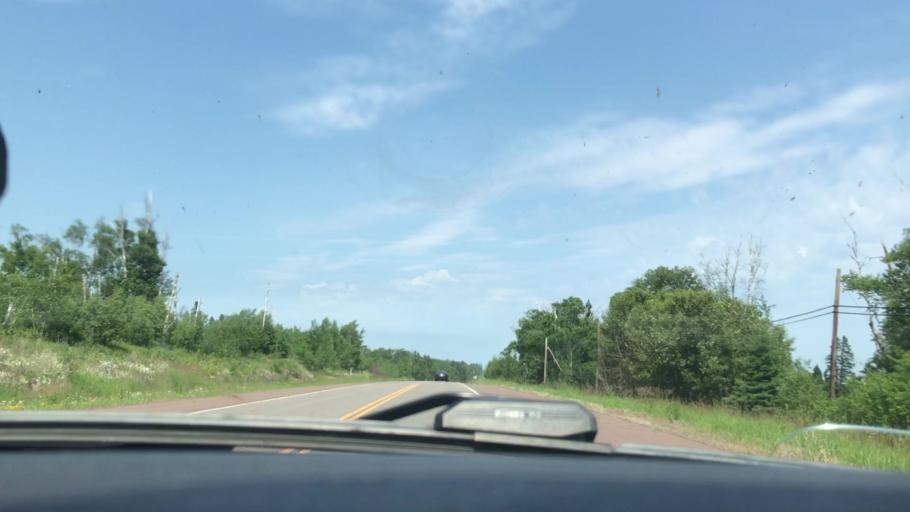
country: US
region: Minnesota
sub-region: Cook County
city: Grand Marais
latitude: 47.5843
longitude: -90.8165
